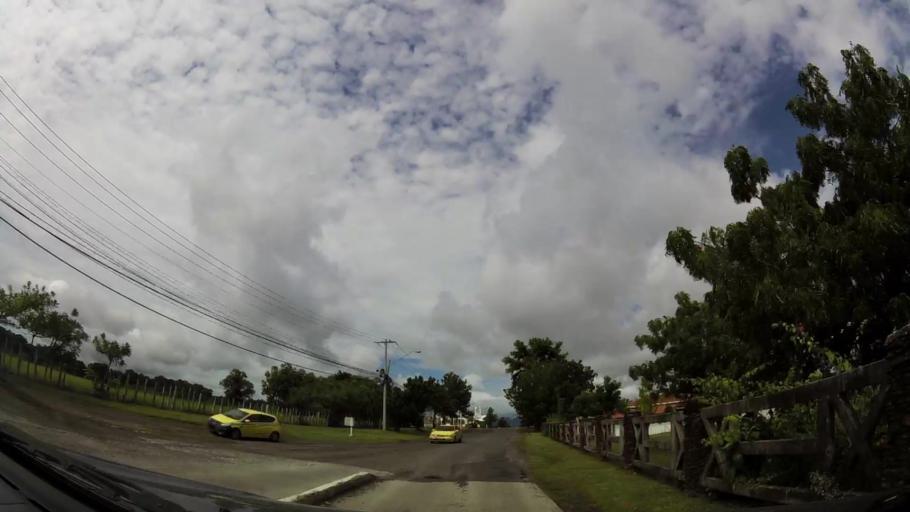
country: PA
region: Panama
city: Nueva Gorgona
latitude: 8.5378
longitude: -79.9063
